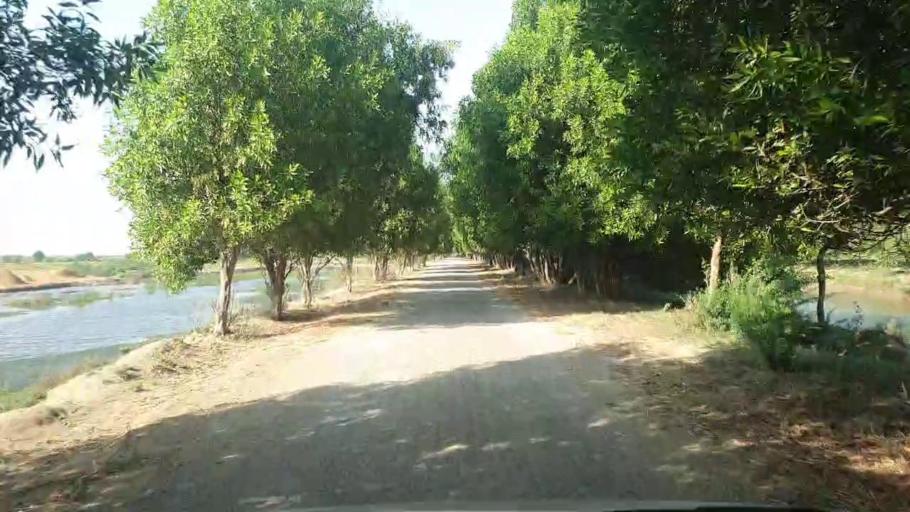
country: PK
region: Sindh
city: Badin
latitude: 24.6235
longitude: 68.8148
